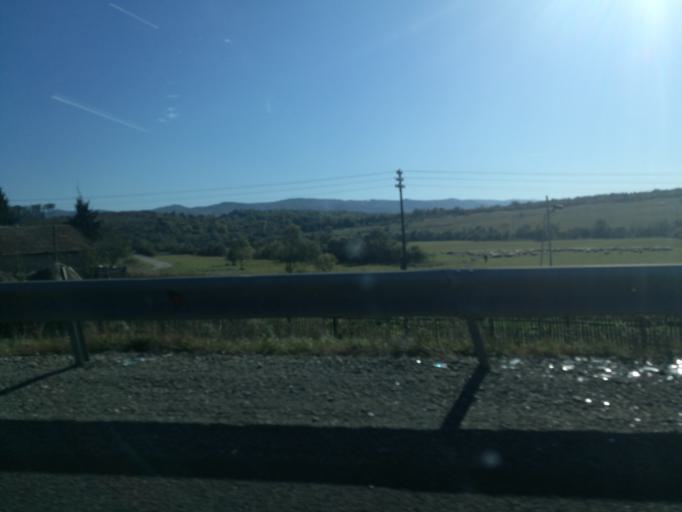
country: RO
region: Brasov
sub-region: Comuna Dumbravita
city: Dumbravita
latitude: 45.7714
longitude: 25.3549
